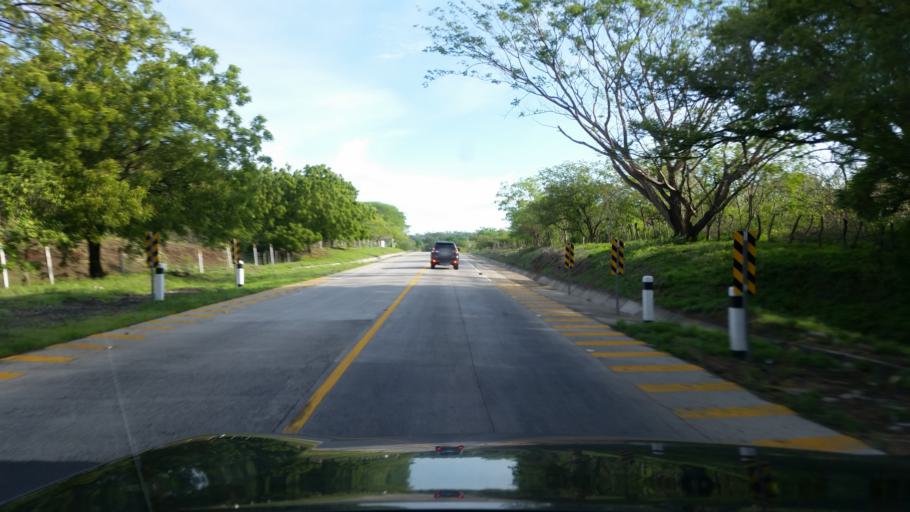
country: NI
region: Leon
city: Nagarote
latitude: 12.1514
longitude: -86.6538
